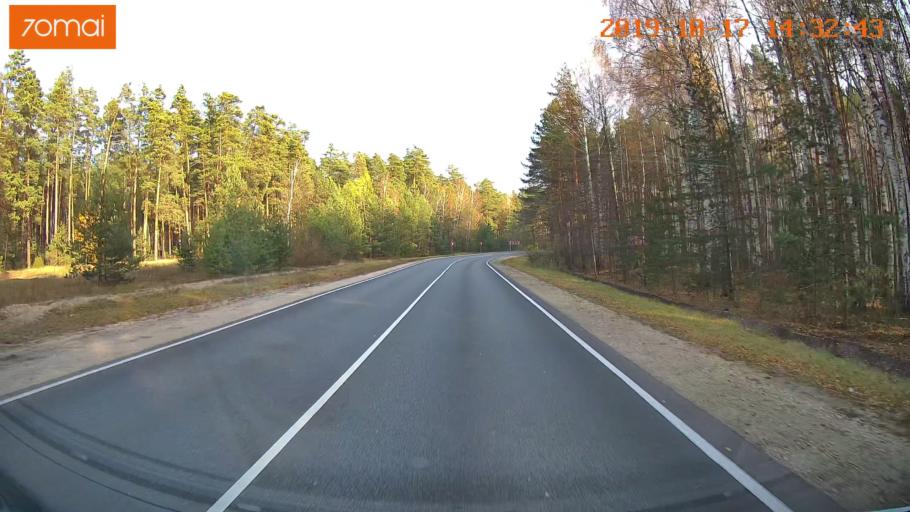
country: RU
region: Rjazan
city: Solotcha
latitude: 54.9269
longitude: 39.9848
